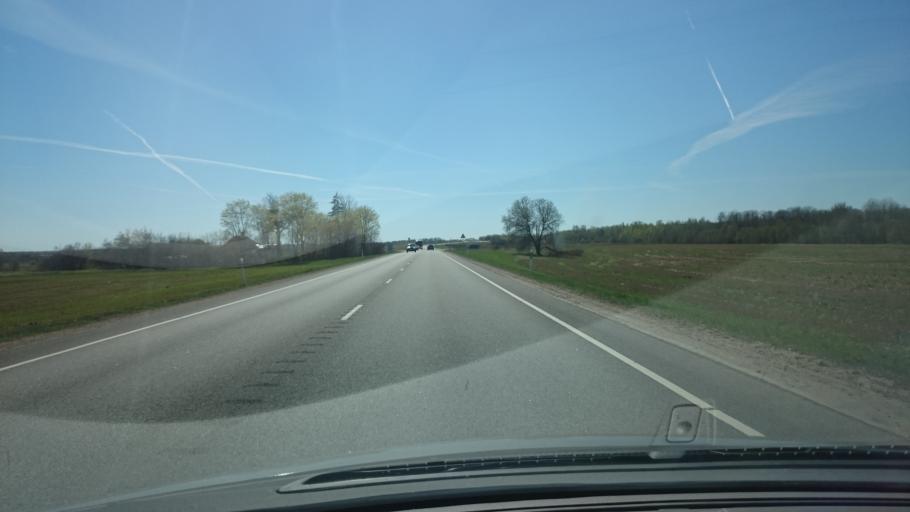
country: EE
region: Ida-Virumaa
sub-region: Narva-Joesuu linn
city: Narva-Joesuu
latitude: 59.4002
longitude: 28.0111
